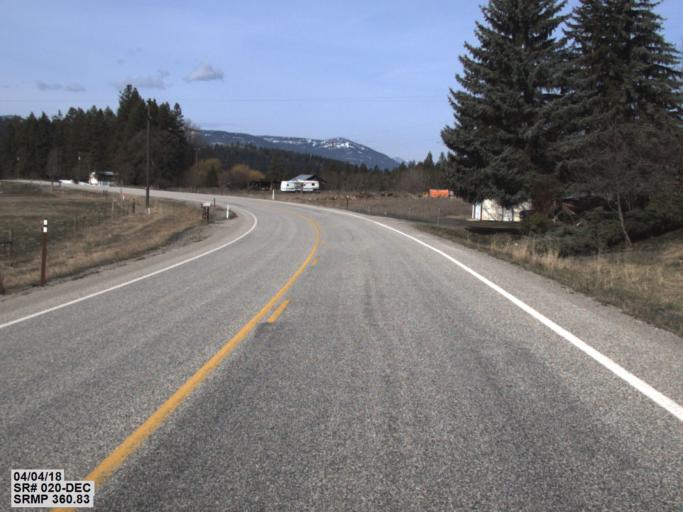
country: US
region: Washington
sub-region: Stevens County
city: Colville
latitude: 48.5161
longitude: -117.7917
